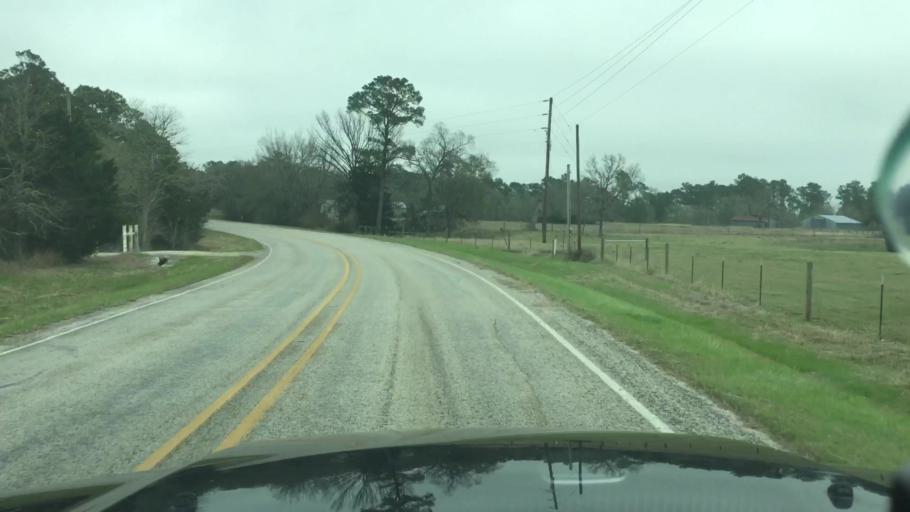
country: US
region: Texas
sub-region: Fayette County
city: La Grange
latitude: 30.0123
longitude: -96.9287
